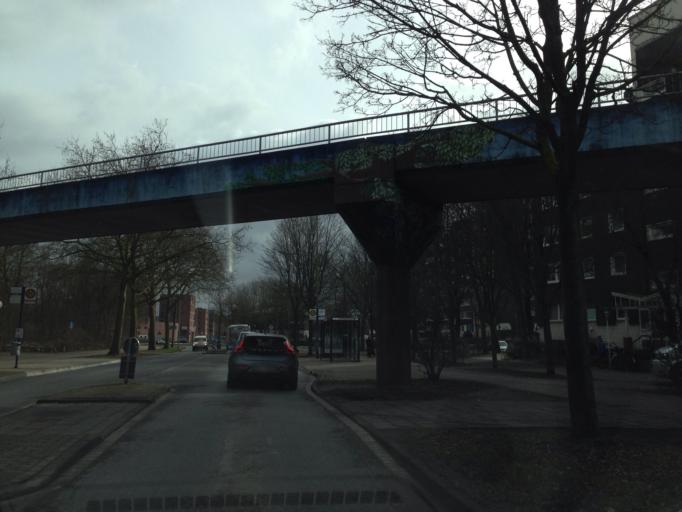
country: DE
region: North Rhine-Westphalia
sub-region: Regierungsbezirk Munster
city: Muenster
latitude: 51.9981
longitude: 7.5981
